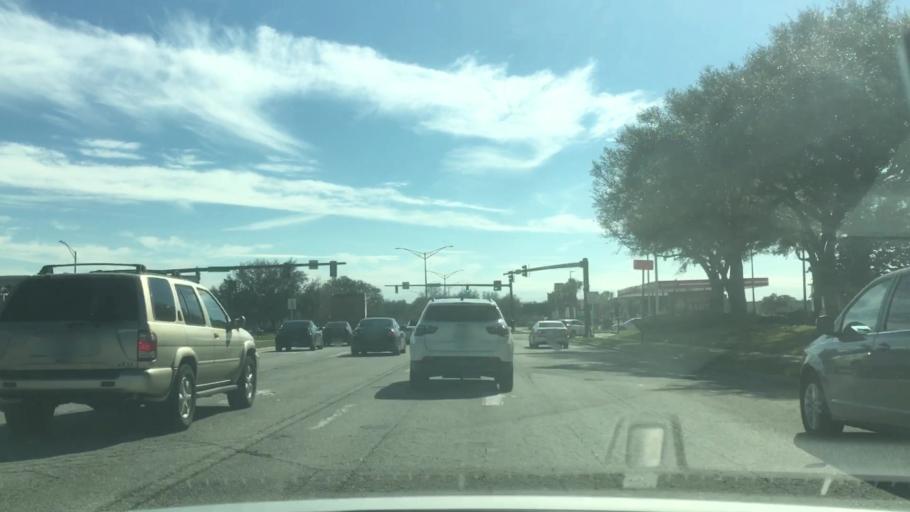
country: US
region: Florida
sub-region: Duval County
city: Jacksonville
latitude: 30.2486
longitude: -81.5361
